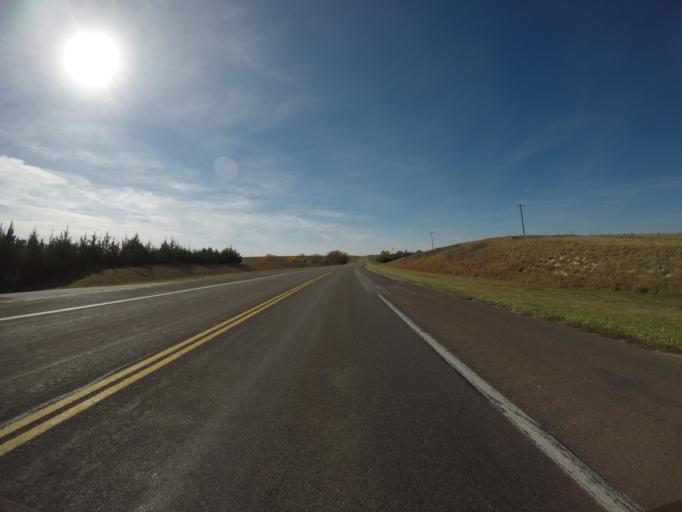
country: US
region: Kansas
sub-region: Norton County
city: Norton
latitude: 39.8277
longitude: -99.9163
